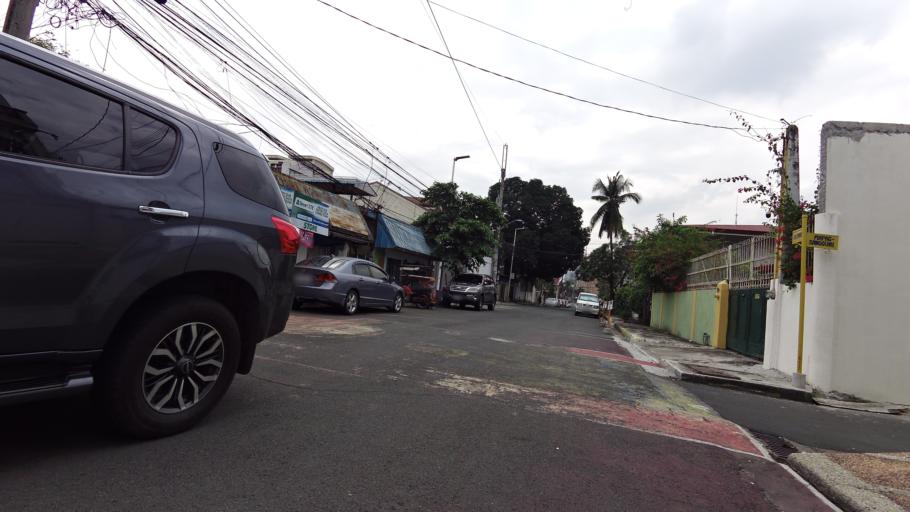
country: PH
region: Metro Manila
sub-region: Quezon City
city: Quezon City
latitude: 14.6375
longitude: 121.0563
